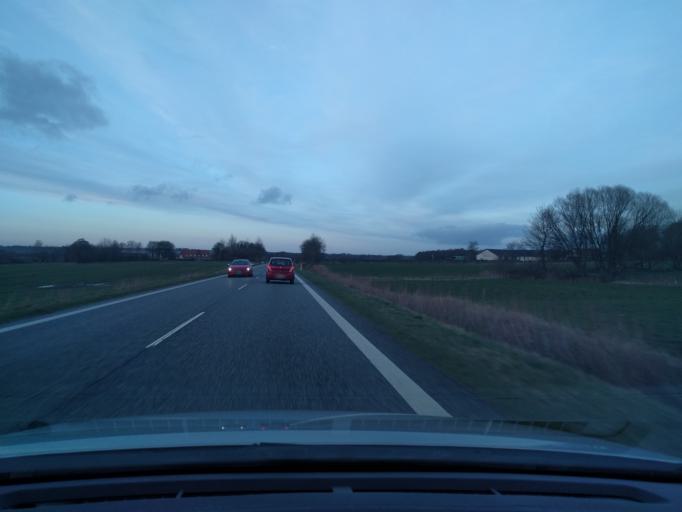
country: DK
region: South Denmark
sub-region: Tonder Kommune
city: Toftlund
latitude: 55.1550
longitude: 9.0343
